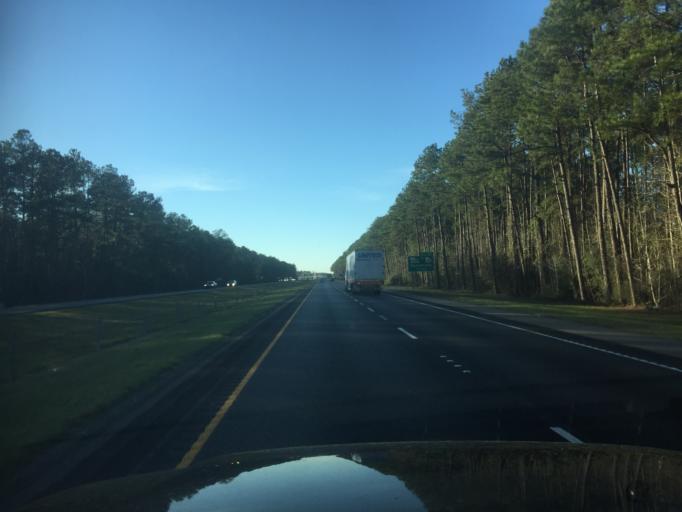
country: US
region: Louisiana
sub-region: Saint Tammany Parish
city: Mandeville
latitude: 30.3863
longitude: -89.9885
